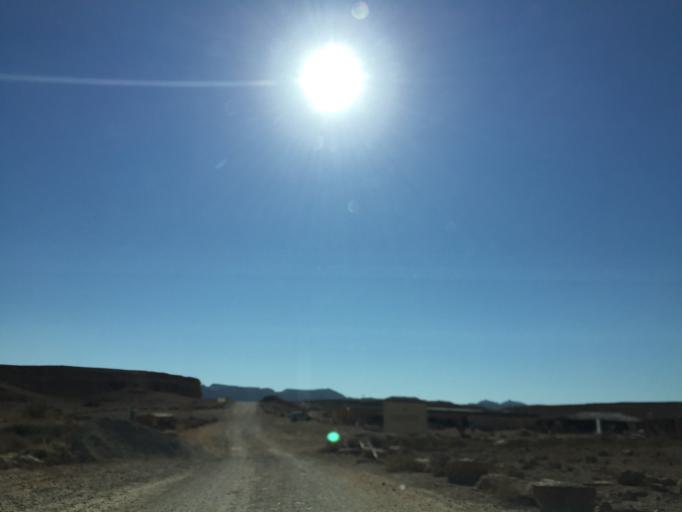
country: IL
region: Southern District
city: Mitzpe Ramon
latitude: 30.6211
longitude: 34.9209
